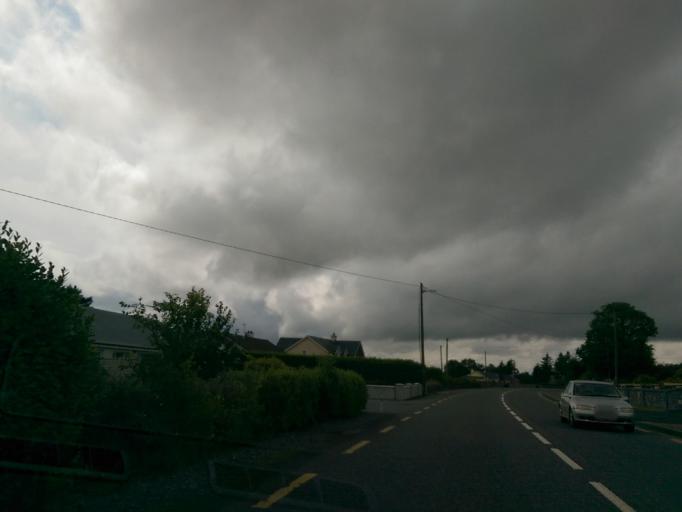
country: IE
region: Munster
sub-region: An Clar
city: Ennis
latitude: 52.7465
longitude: -9.1532
